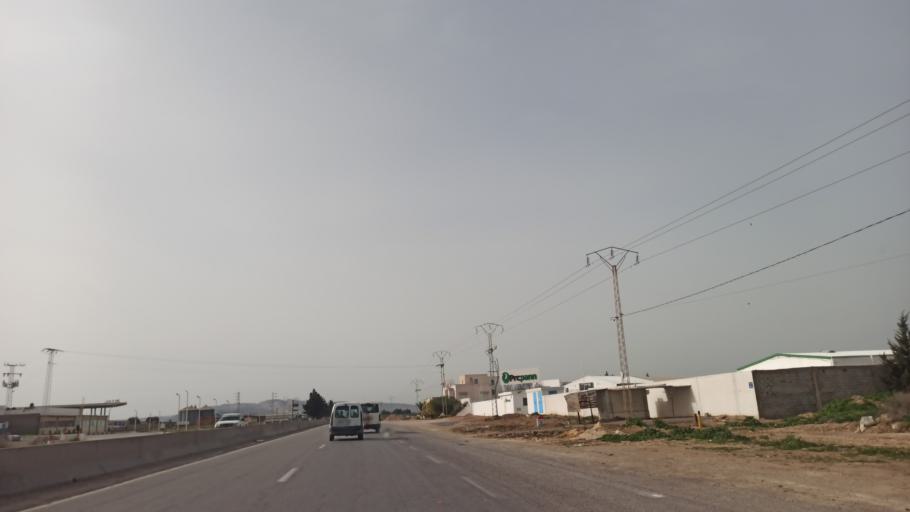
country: TN
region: Tunis
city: La Mohammedia
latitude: 36.5850
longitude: 10.0993
